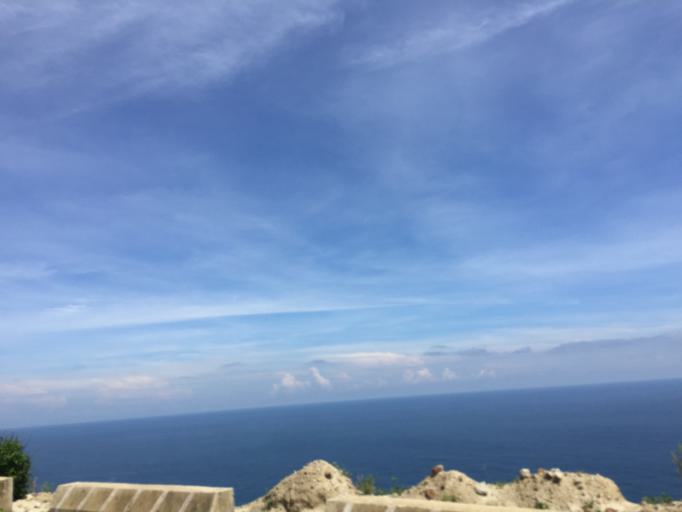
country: VN
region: Quang Nam
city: Hoi An
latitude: 15.9737
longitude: 108.5085
